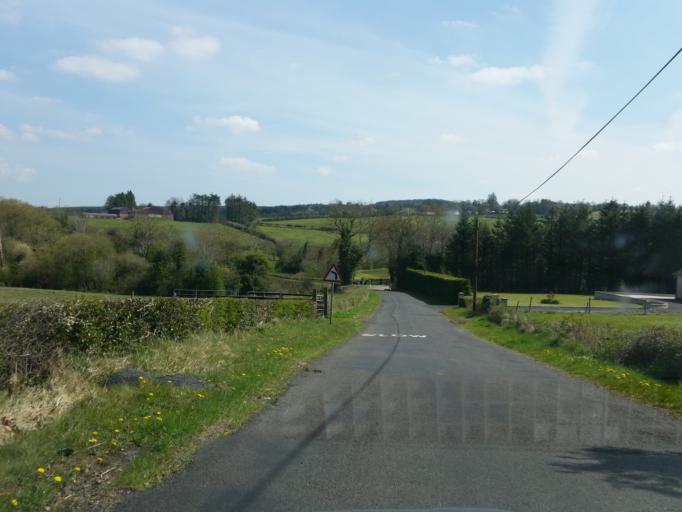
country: GB
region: Northern Ireland
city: Fivemiletown
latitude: 54.3096
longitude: -7.3685
